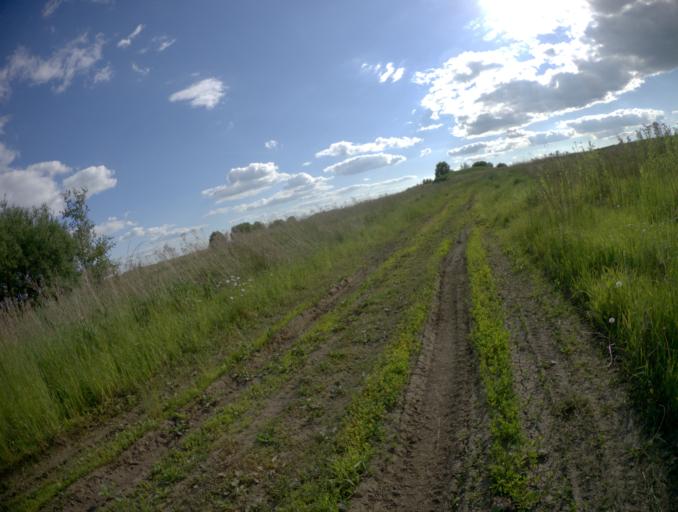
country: RU
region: Vladimir
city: Vladimir
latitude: 56.2814
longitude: 40.2620
